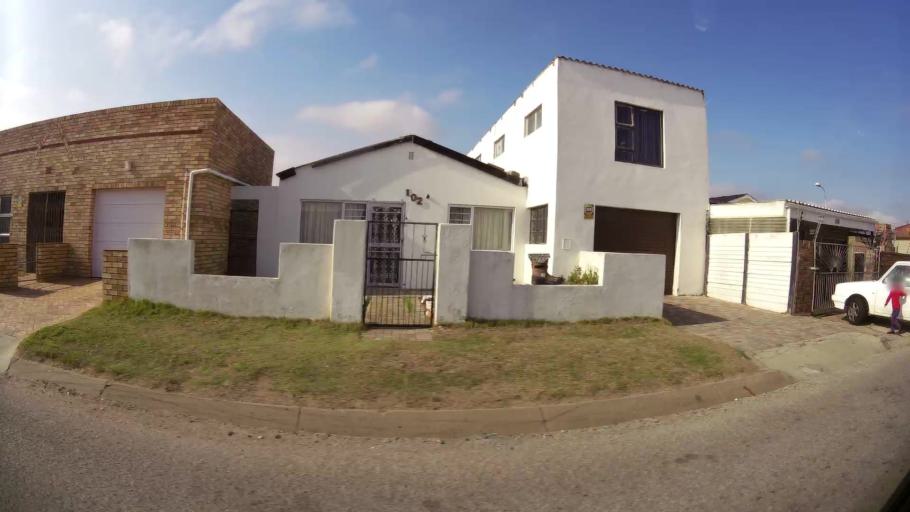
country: ZA
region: Eastern Cape
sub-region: Nelson Mandela Bay Metropolitan Municipality
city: Port Elizabeth
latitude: -33.9178
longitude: 25.5348
